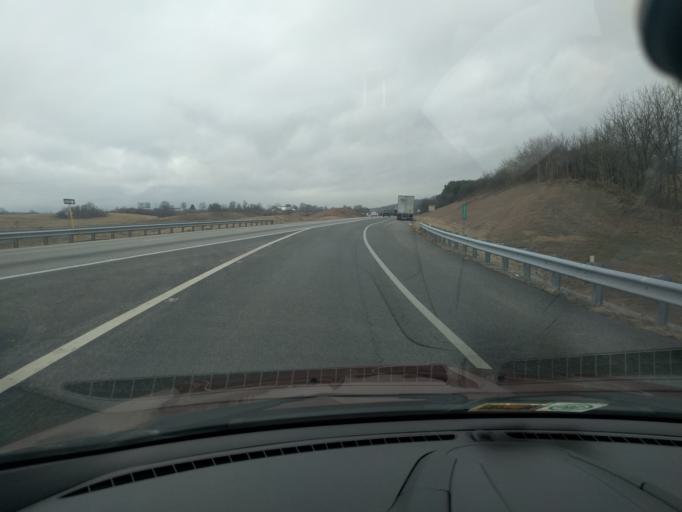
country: US
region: Virginia
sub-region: Augusta County
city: Jolivue
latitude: 38.1069
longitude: -79.0634
